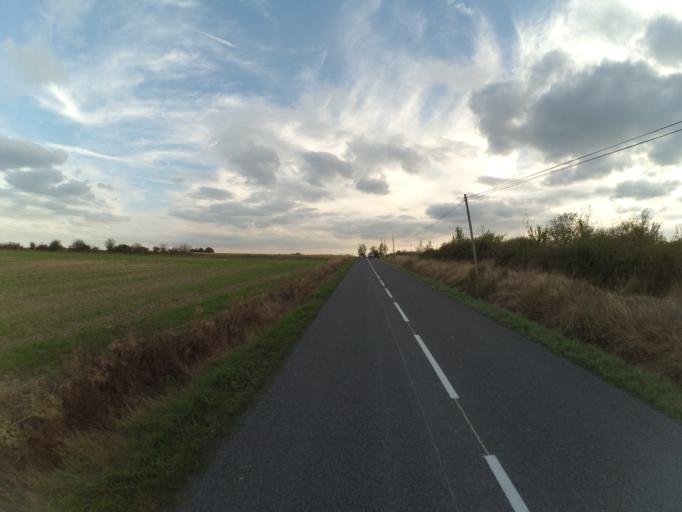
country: FR
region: Centre
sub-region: Departement d'Indre-et-Loire
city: Nazelles-Negron
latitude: 47.4477
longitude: 0.9514
